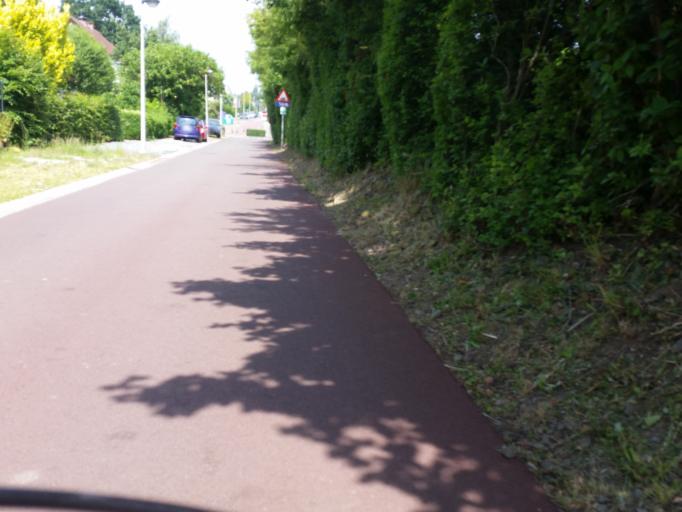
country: BE
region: Flanders
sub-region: Provincie Antwerpen
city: Hove
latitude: 51.1431
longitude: 4.4712
